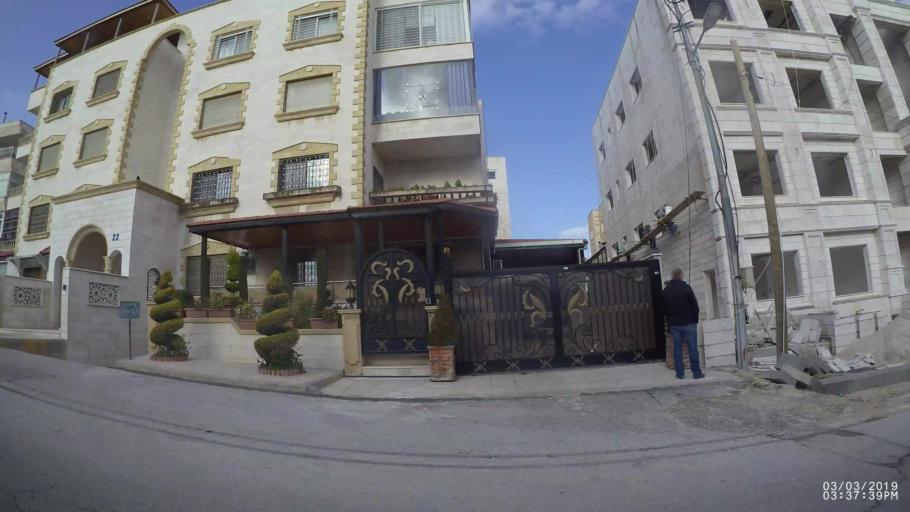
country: JO
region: Amman
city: Al Jubayhah
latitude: 31.9787
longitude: 35.8851
